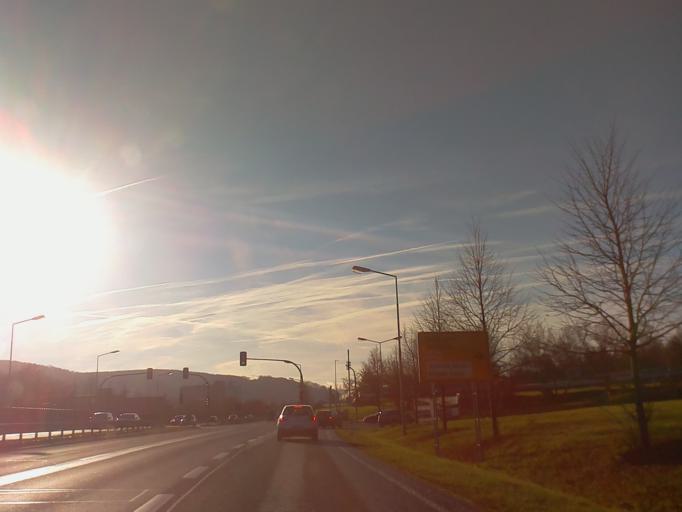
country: DE
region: Thuringia
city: Rudolstadt
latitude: 50.6995
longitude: 11.3256
